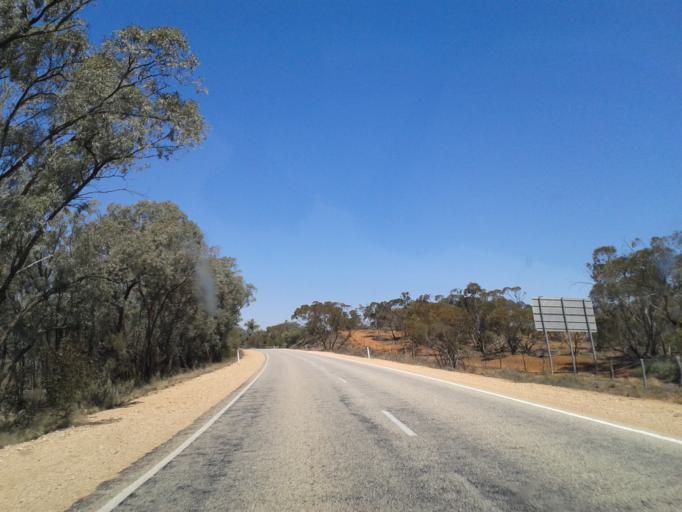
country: AU
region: Victoria
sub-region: Swan Hill
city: Swan Hill
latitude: -34.7485
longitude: 143.1854
